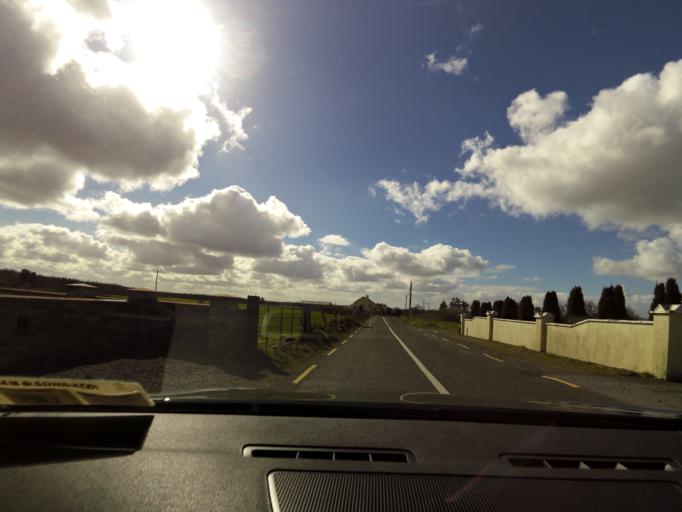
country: IE
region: Connaught
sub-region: County Galway
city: Athenry
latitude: 53.4186
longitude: -8.6100
